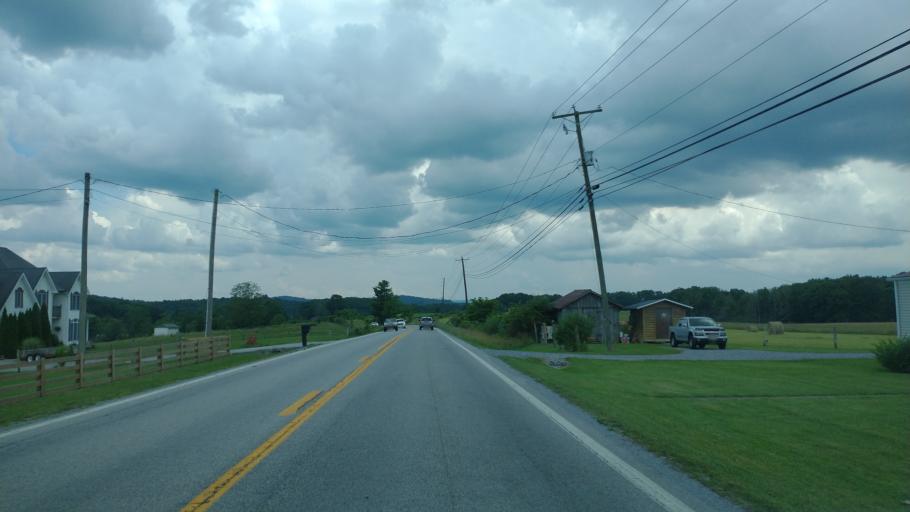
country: US
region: West Virginia
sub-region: Mercer County
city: Athens
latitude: 37.4516
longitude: -81.0075
